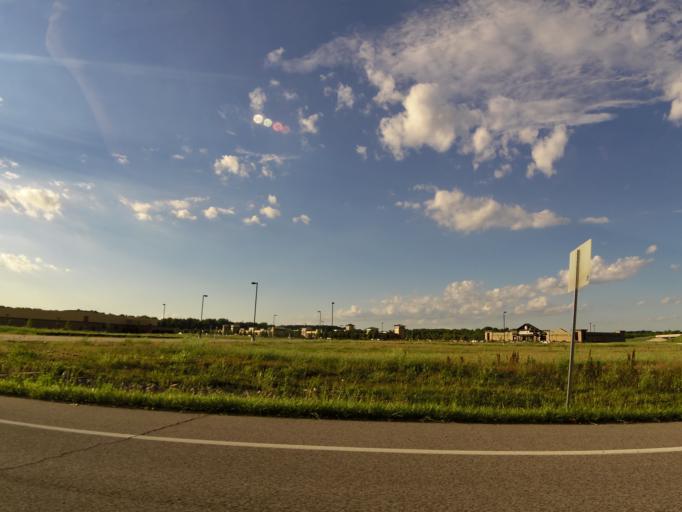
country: US
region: Missouri
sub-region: Saint Charles County
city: Weldon Spring
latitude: 38.6720
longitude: -90.6608
